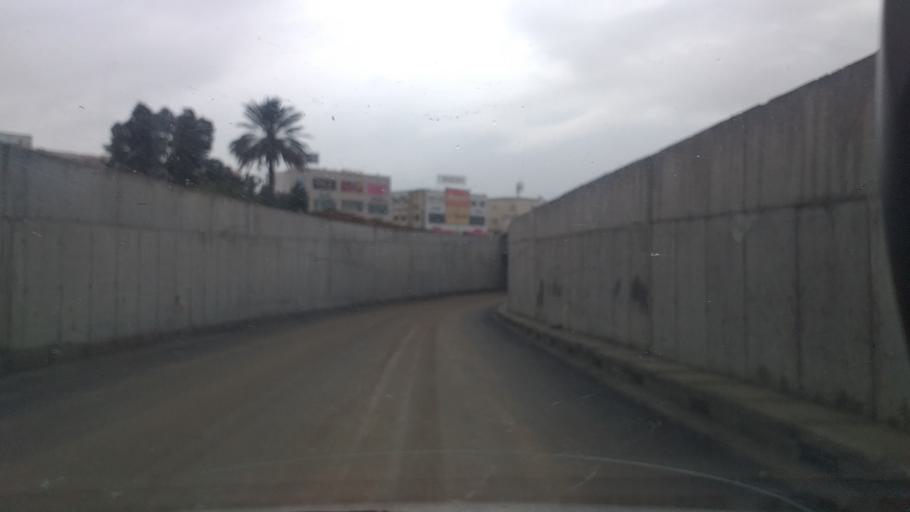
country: TN
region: Ariana
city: Ariana
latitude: 36.8681
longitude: 10.2276
